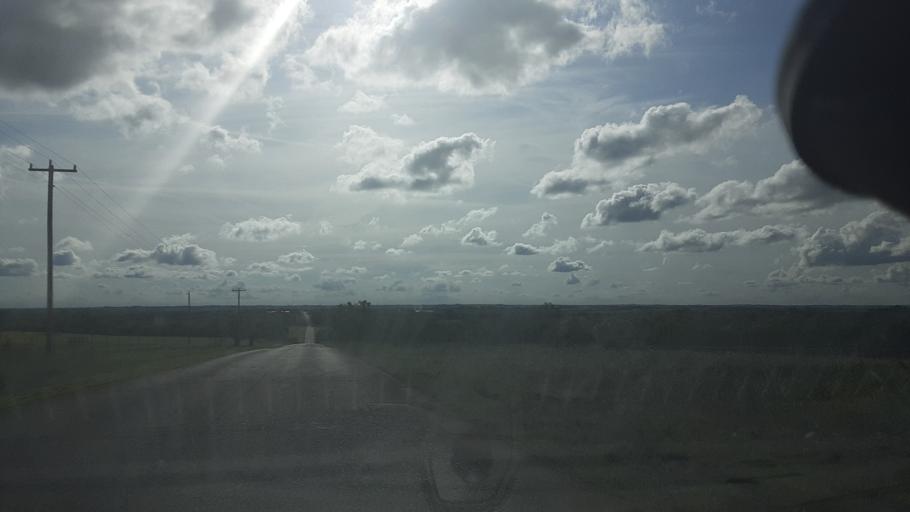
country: US
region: Oklahoma
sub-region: Logan County
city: Langston
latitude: 36.0578
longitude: -97.3633
